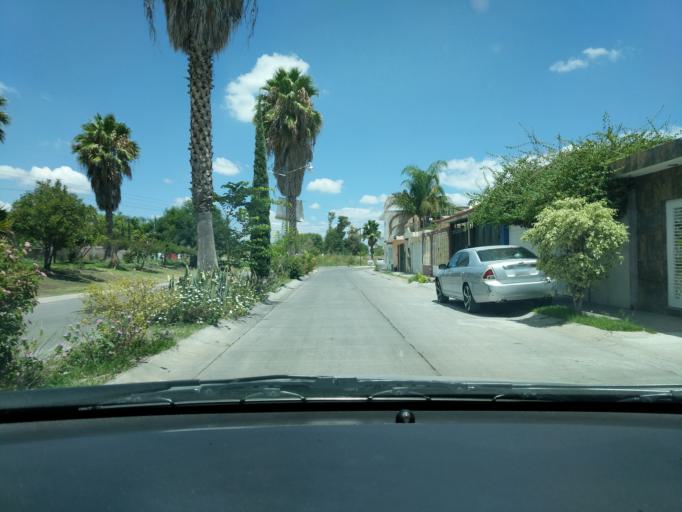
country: MX
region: Guanajuato
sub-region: Salamanca
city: El Divisador
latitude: 20.5985
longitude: -101.1714
